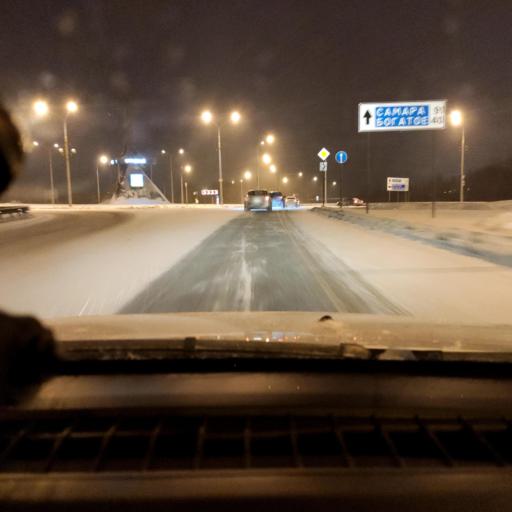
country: RU
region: Samara
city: Otradnyy
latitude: 53.3511
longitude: 51.3282
